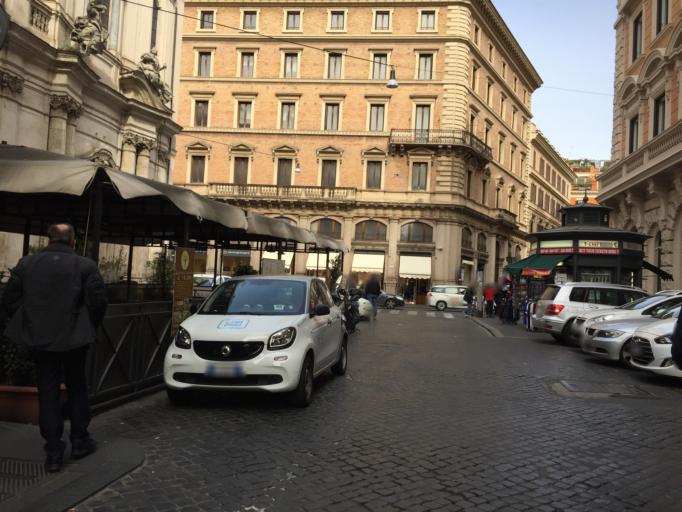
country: VA
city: Vatican City
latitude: 41.9016
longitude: 12.4828
